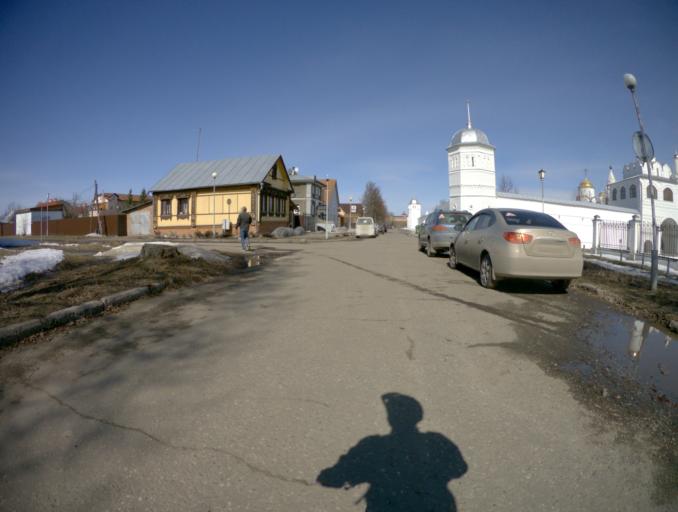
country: RU
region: Vladimir
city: Suzdal'
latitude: 56.4281
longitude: 40.4352
